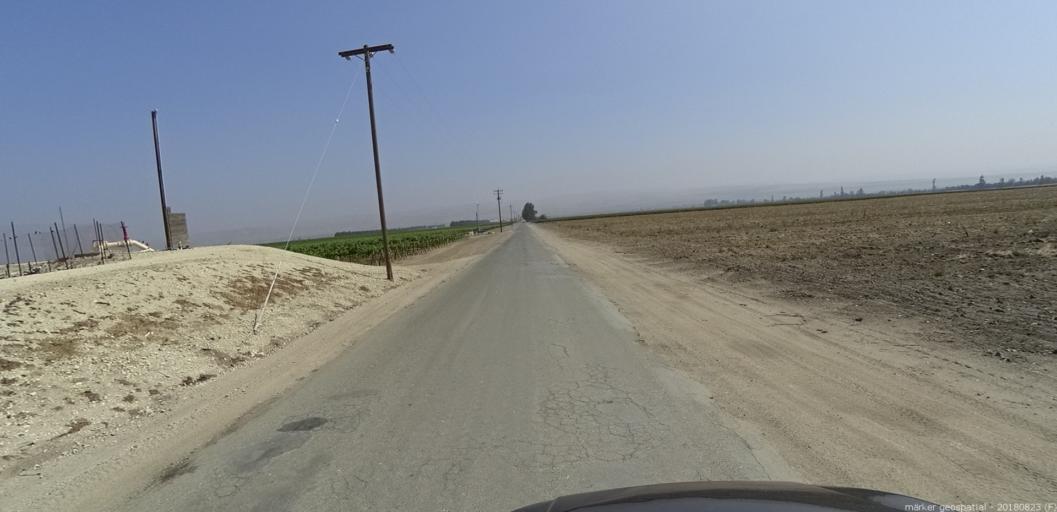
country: US
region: California
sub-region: Monterey County
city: Greenfield
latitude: 36.2628
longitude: -121.2092
